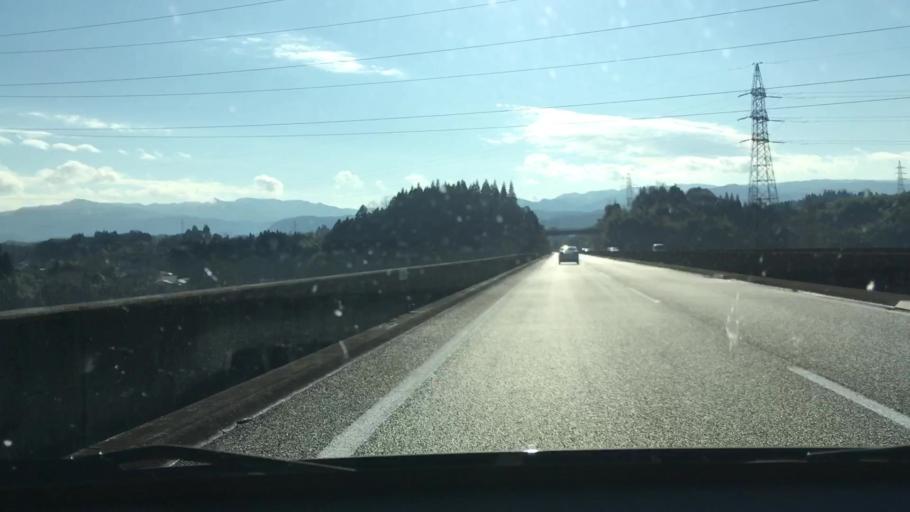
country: JP
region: Kumamoto
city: Hitoyoshi
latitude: 32.2147
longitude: 130.7781
